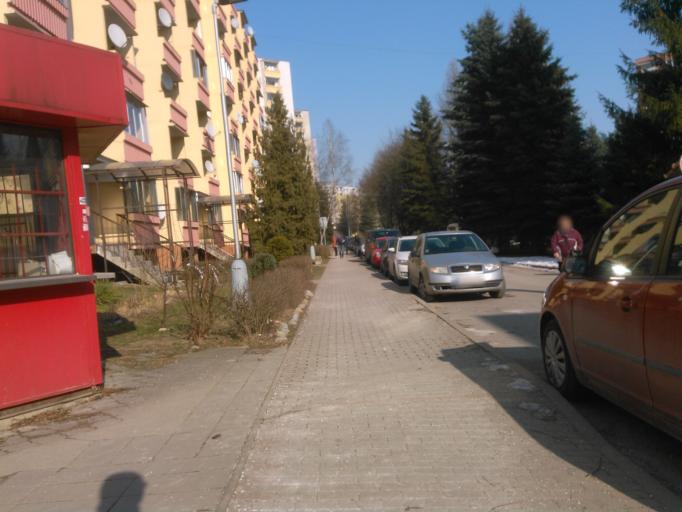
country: SK
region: Zilinsky
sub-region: Okres Dolny Kubin
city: Dolny Kubin
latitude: 49.2112
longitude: 19.2828
